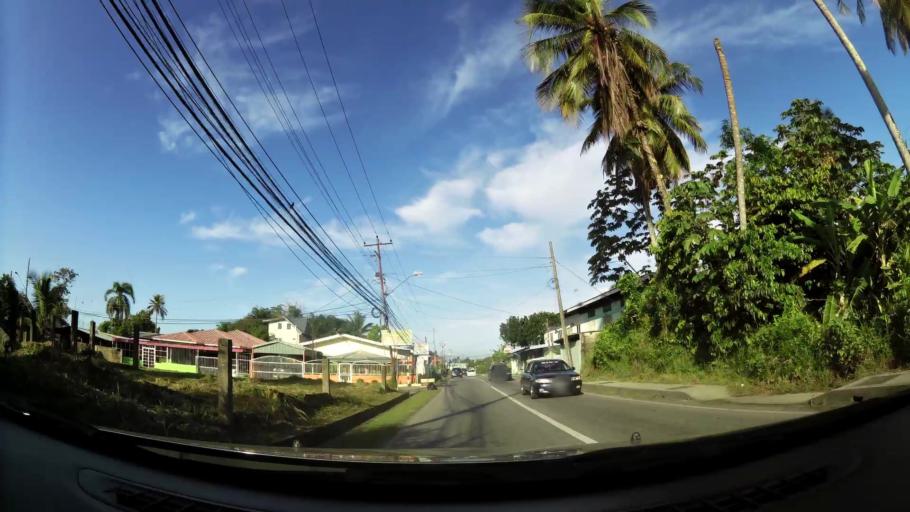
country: TT
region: Chaguanas
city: Chaguanas
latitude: 10.5469
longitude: -61.3475
